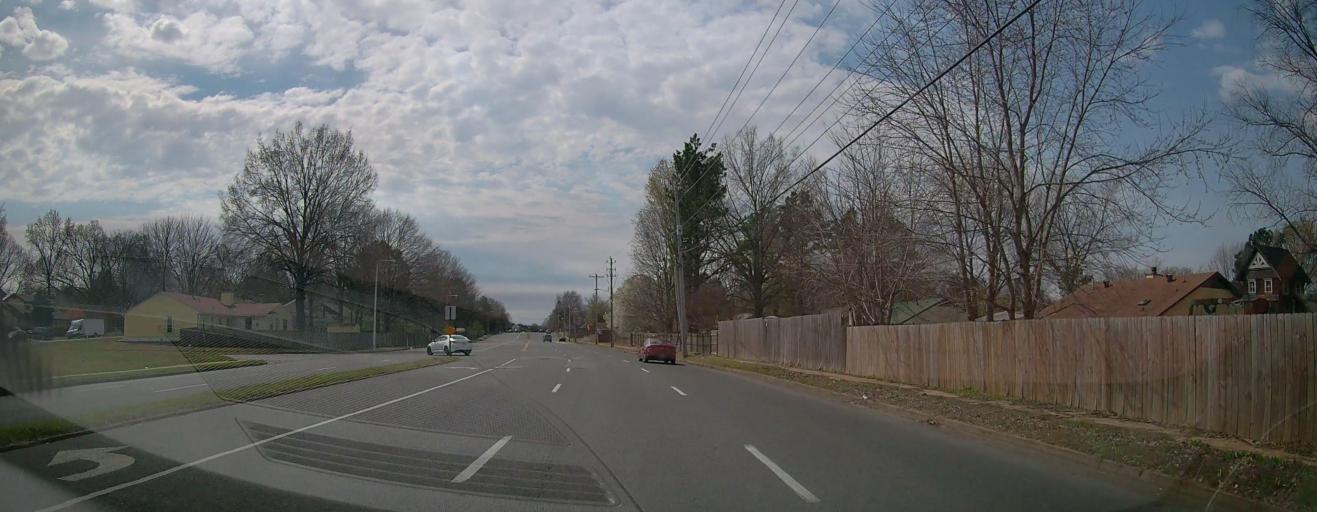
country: US
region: Tennessee
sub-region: Shelby County
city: Germantown
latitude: 35.0324
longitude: -89.8481
